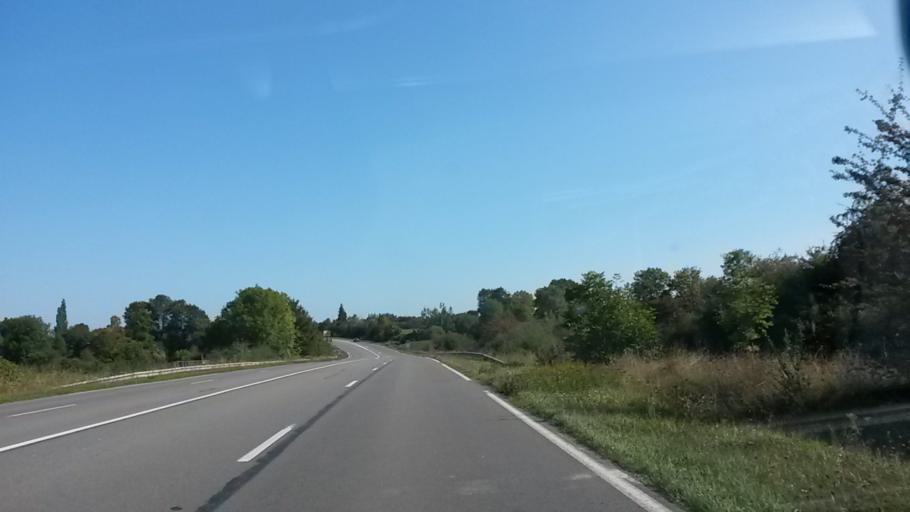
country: FR
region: Picardie
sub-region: Departement de l'Aisne
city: La Flamengrie
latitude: 50.0529
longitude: 3.9298
